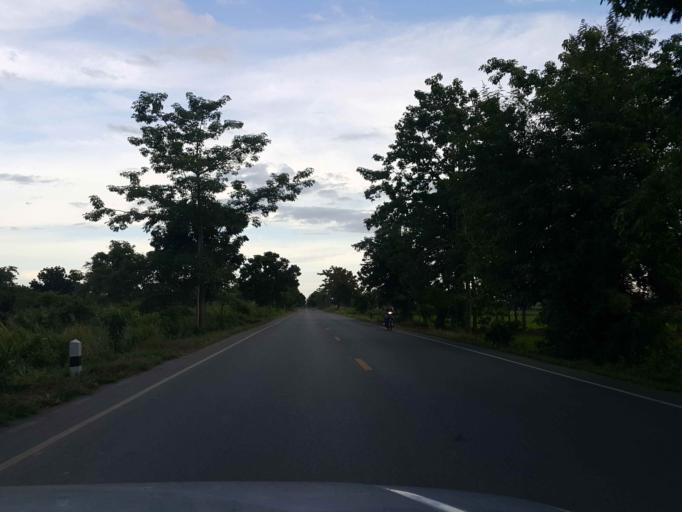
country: TH
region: Sukhothai
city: Sawankhalok
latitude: 17.3689
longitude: 99.7416
